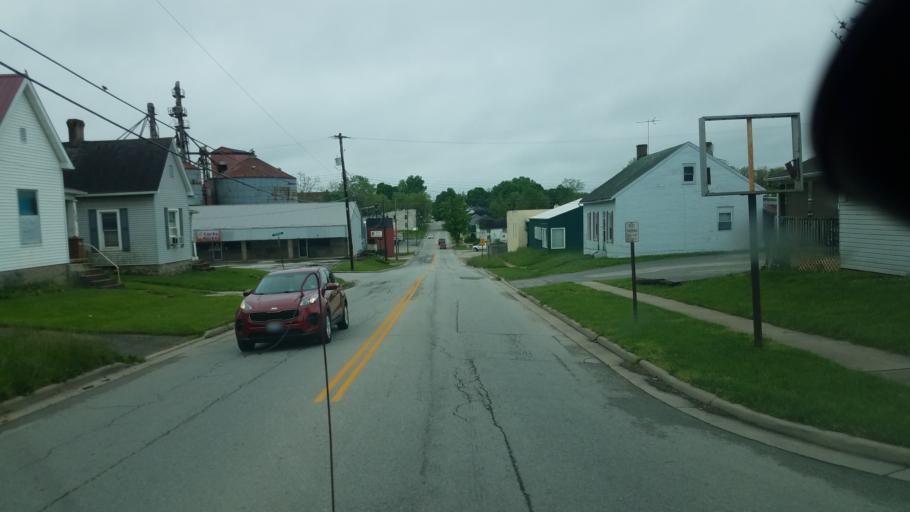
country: US
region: Ohio
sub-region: Highland County
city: Hillsboro
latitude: 39.2084
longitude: -83.6126
